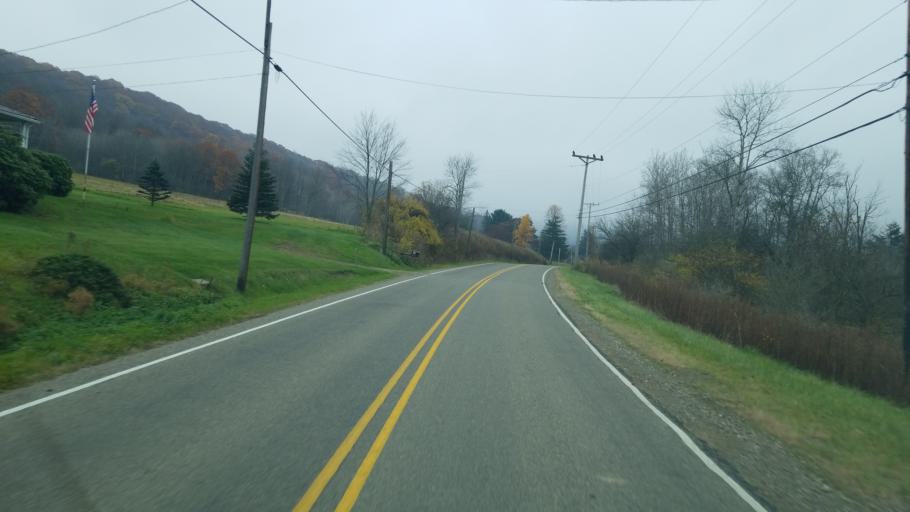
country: US
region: Pennsylvania
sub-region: McKean County
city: Smethport
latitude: 41.8702
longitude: -78.4777
